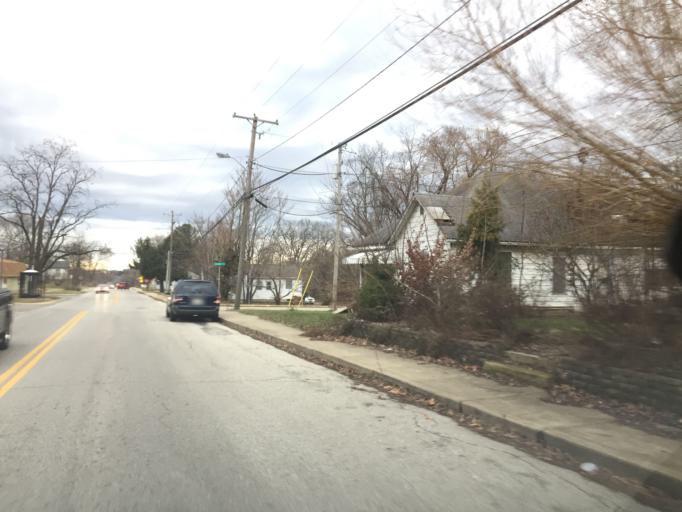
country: US
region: Indiana
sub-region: Monroe County
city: Bloomington
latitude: 39.1733
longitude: -86.5487
